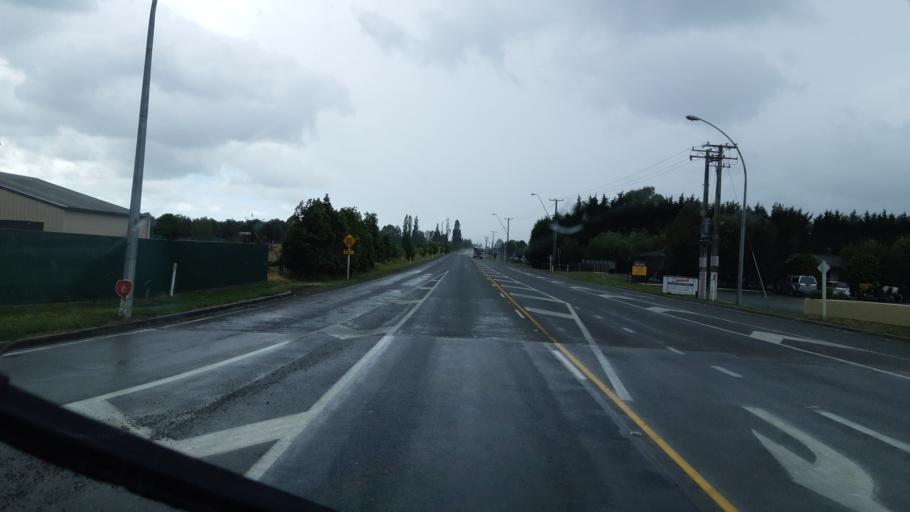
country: NZ
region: Tasman
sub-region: Tasman District
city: Brightwater
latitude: -41.3797
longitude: 173.1133
